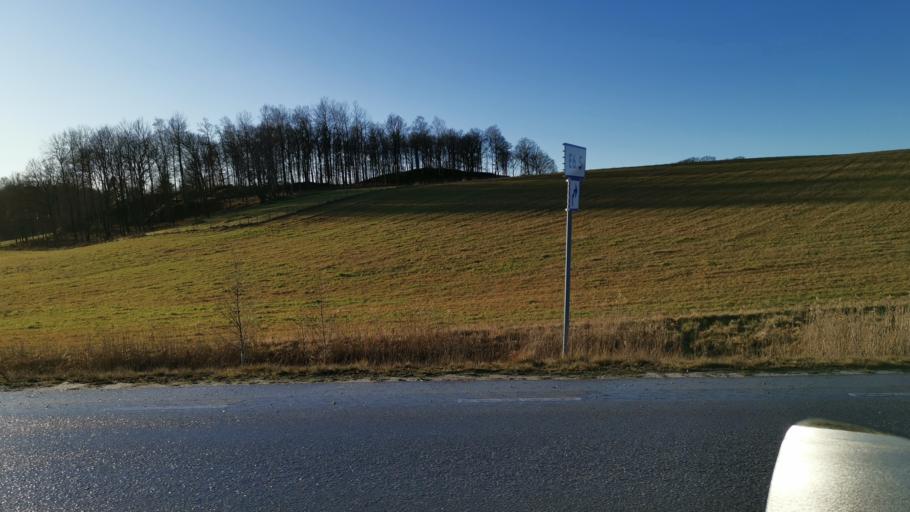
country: SE
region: Vaestra Goetaland
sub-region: Munkedals Kommun
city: Munkedal
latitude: 58.4737
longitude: 11.6597
